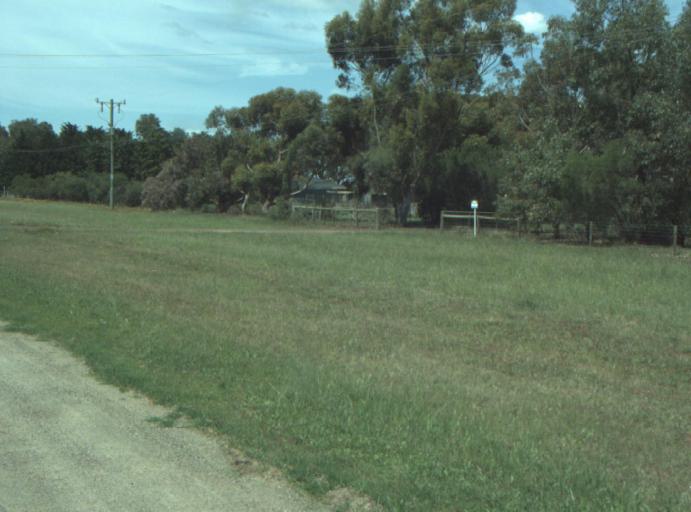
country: AU
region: Victoria
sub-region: Greater Geelong
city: Lara
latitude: -38.0098
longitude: 144.3838
